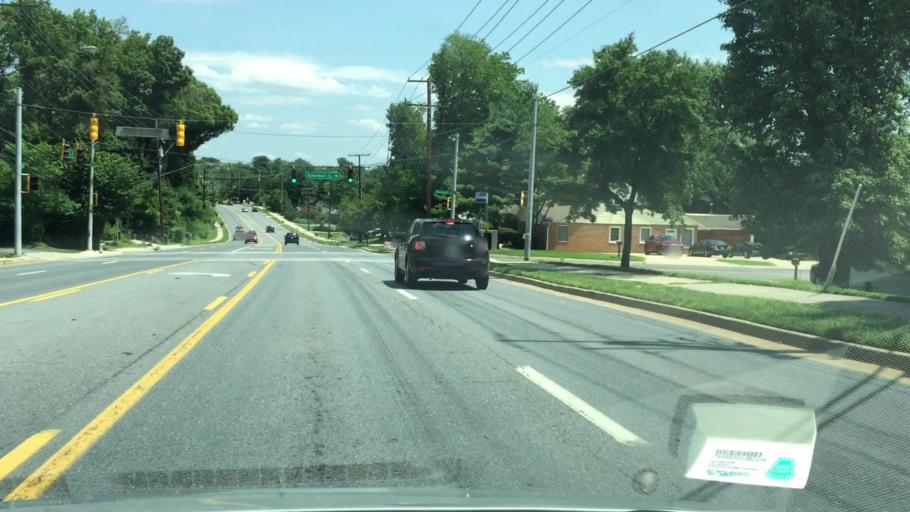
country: US
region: Maryland
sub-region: Montgomery County
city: Leisure World
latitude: 39.0907
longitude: -77.0597
